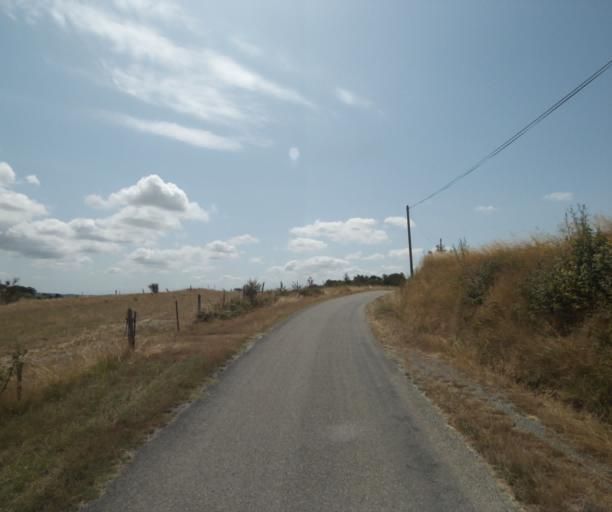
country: FR
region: Midi-Pyrenees
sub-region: Departement de la Haute-Garonne
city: Saint-Felix-Lauragais
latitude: 43.4412
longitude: 1.8880
